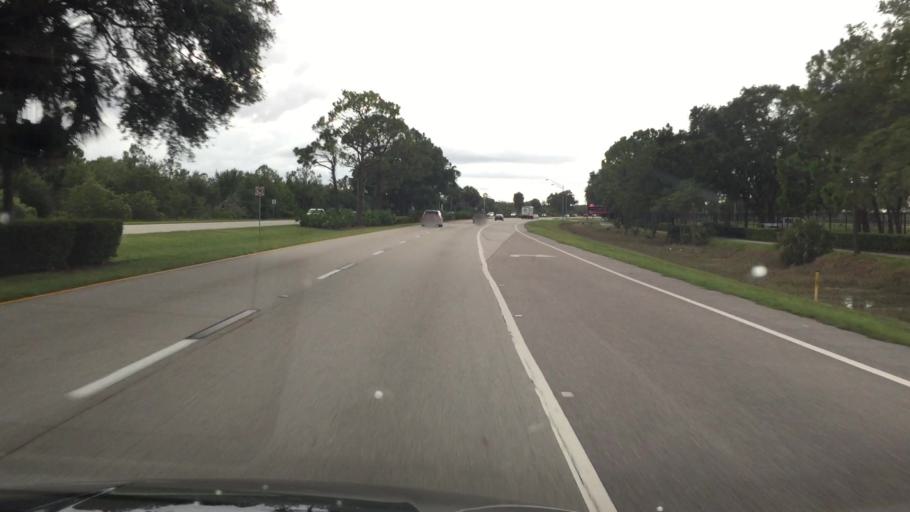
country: US
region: Florida
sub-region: Lee County
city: Villas
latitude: 26.5377
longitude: -81.8405
